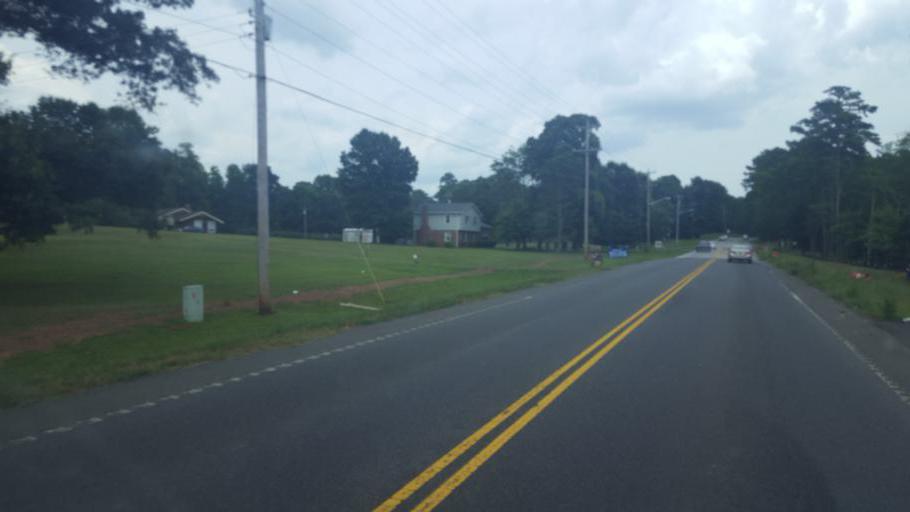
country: US
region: South Carolina
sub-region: York County
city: Newport
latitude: 34.9568
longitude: -81.1022
